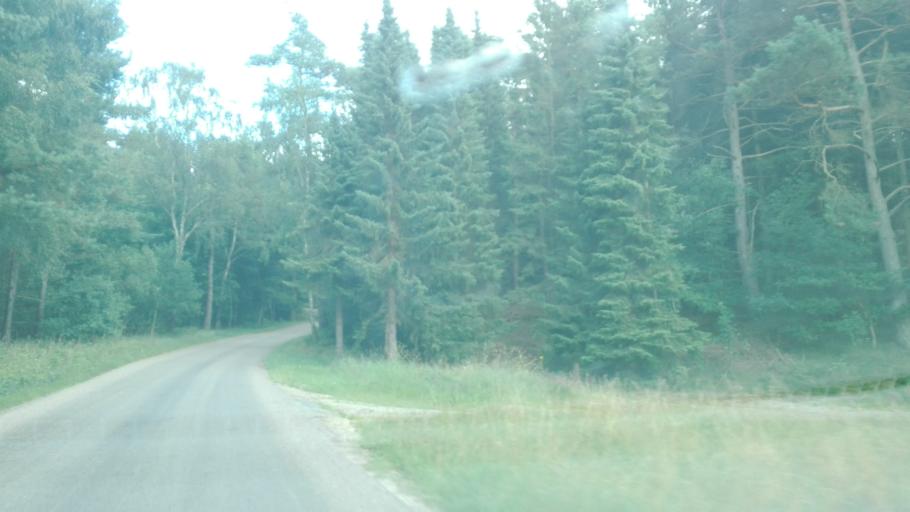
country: DK
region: Central Jutland
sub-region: Silkeborg Kommune
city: Svejbaek
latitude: 56.0810
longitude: 9.6062
